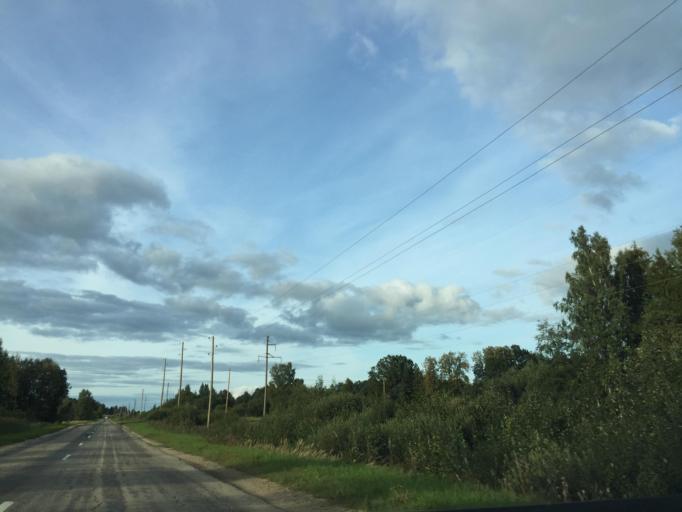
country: LV
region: Nereta
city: Nereta
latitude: 56.2374
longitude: 25.3271
